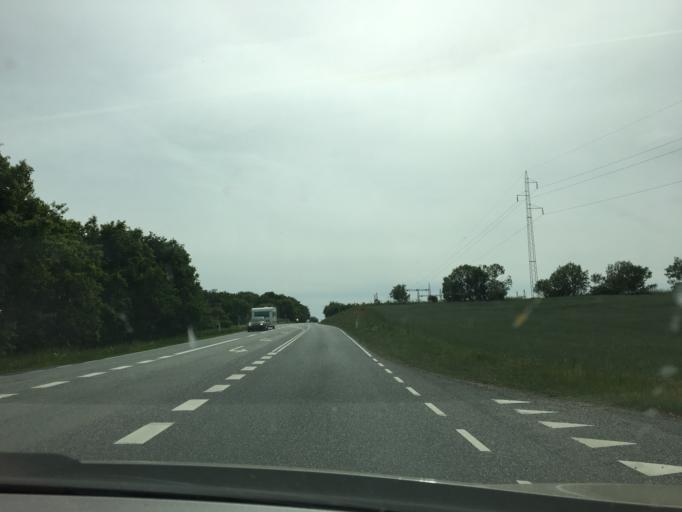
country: DK
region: Central Jutland
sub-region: Norddjurs Kommune
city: Allingabro
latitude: 56.4613
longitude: 10.3006
